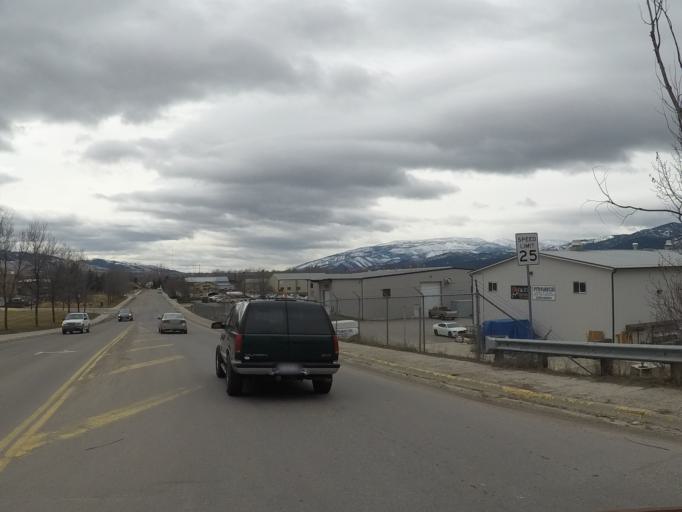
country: US
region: Montana
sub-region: Missoula County
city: Orchard Homes
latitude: 46.8854
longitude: -114.0441
